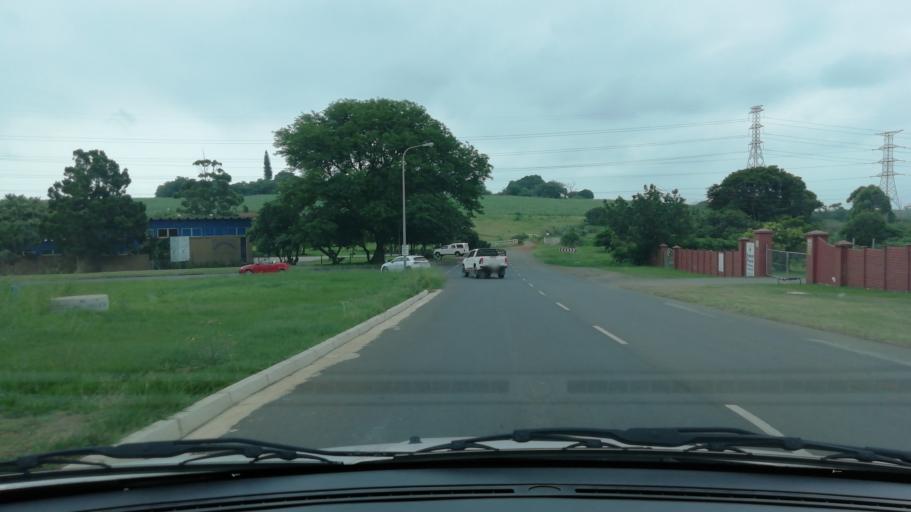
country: ZA
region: KwaZulu-Natal
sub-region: uThungulu District Municipality
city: Empangeni
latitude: -28.7357
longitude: 31.8954
